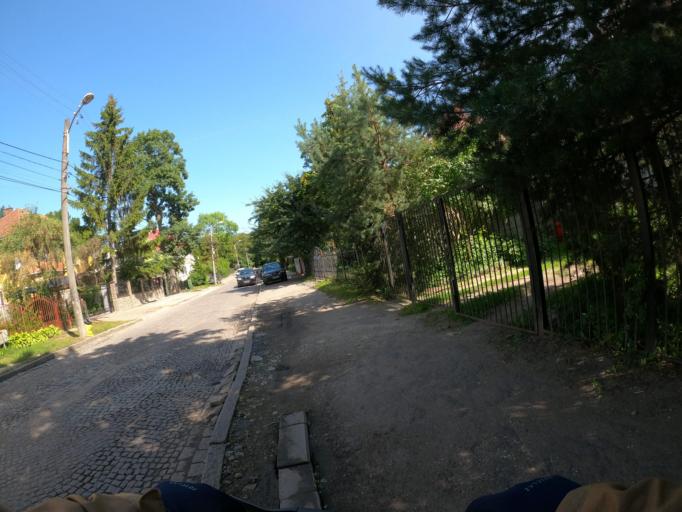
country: RU
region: Kaliningrad
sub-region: Gorod Kaliningrad
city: Kaliningrad
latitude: 54.7361
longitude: 20.5215
